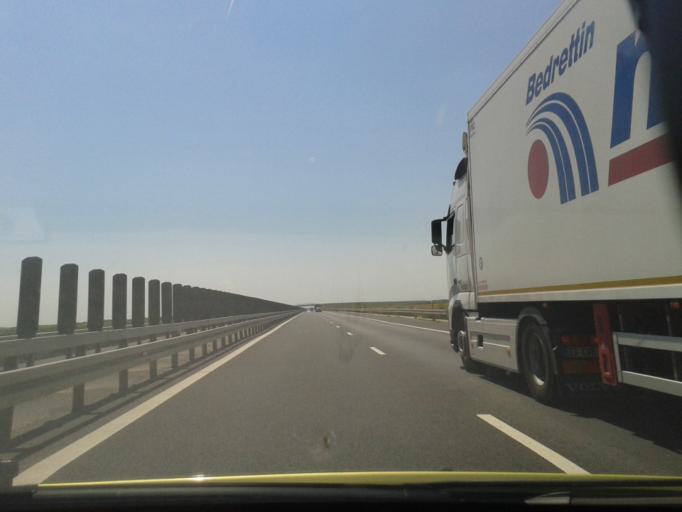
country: RO
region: Timis
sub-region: Comuna Remetea Mare
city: Remetea Mare
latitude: 45.8270
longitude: 21.3651
